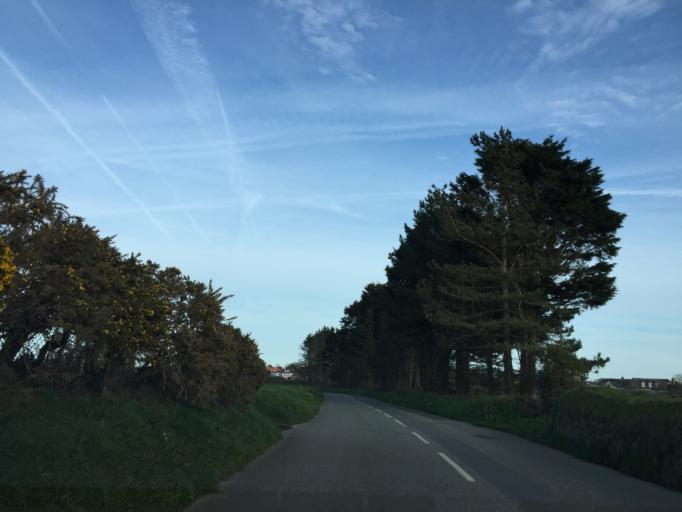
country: JE
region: St Helier
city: Saint Helier
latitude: 49.2456
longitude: -2.1011
